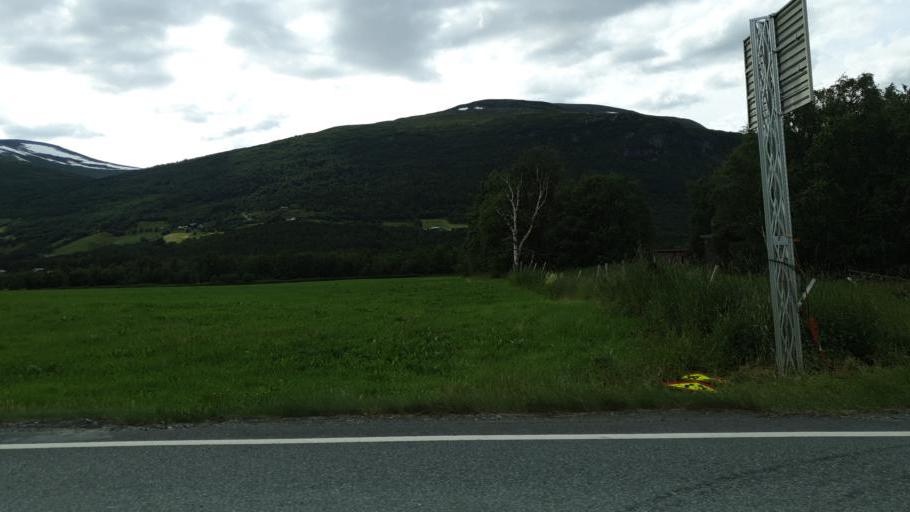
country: NO
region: Sor-Trondelag
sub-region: Oppdal
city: Oppdal
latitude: 62.5454
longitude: 9.6313
